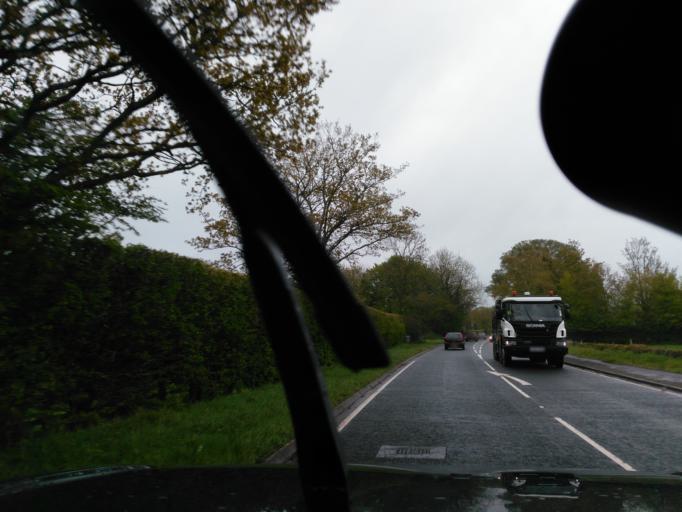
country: GB
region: England
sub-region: Bath and North East Somerset
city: Freshford
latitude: 51.3752
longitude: -2.2829
